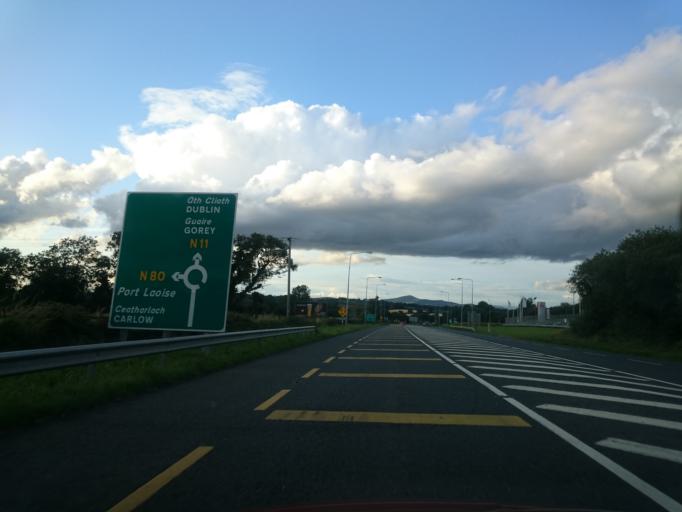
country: IE
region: Leinster
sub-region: Loch Garman
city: Enniscorthy
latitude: 52.5413
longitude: -6.5517
